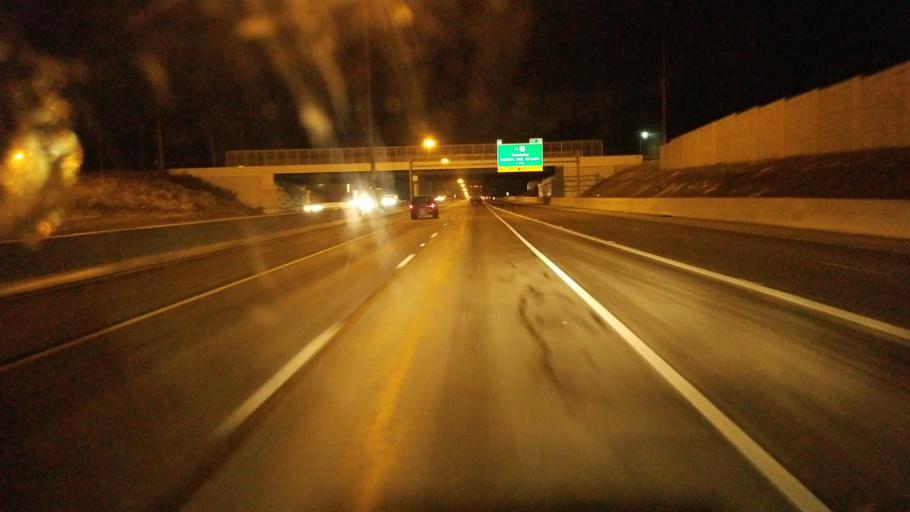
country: US
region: Ohio
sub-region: Montgomery County
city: Vandalia
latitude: 39.8652
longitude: -84.1974
